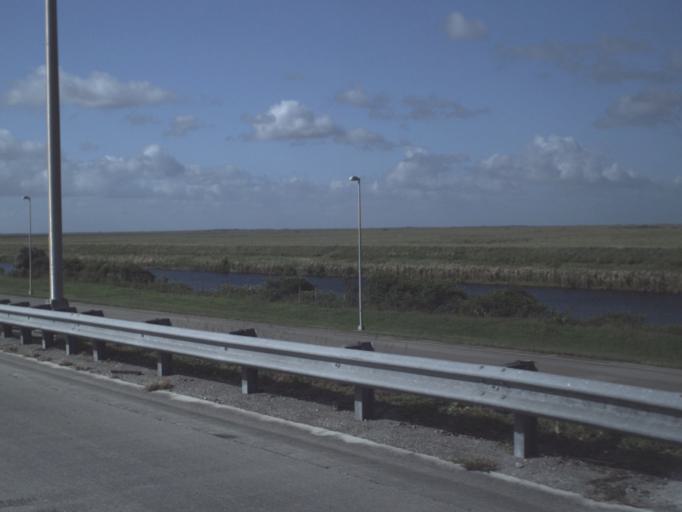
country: US
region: Florida
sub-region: Broward County
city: Coral Springs
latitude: 26.2718
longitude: -80.2969
